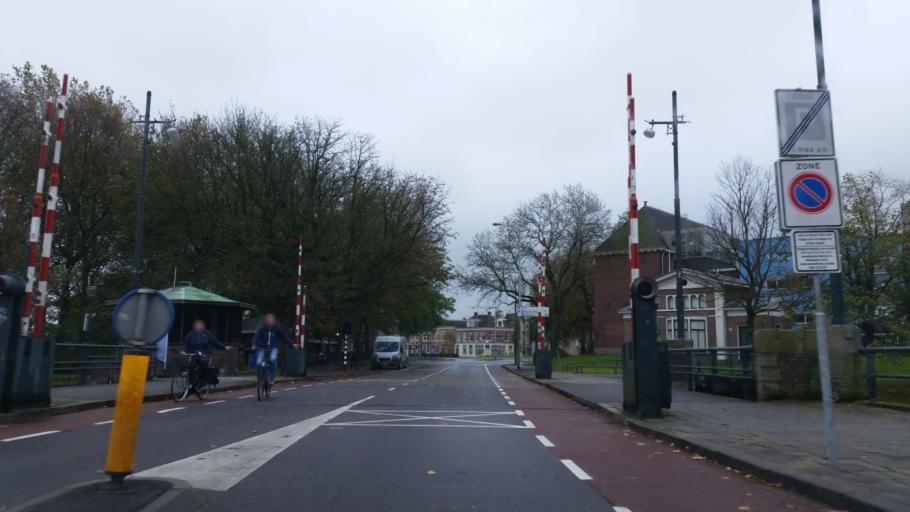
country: NL
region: Friesland
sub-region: Gemeente Leeuwarden
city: Bilgaard
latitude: 53.2064
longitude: 5.7967
